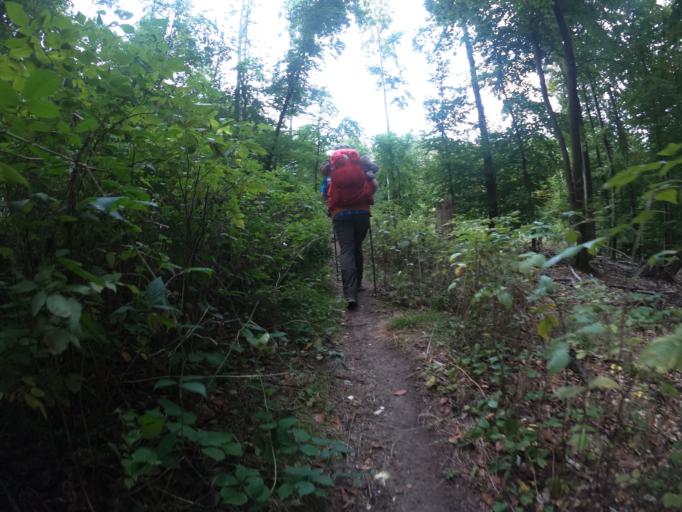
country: DE
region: Hesse
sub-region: Regierungsbezirk Darmstadt
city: Niedernhausen
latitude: 50.1538
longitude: 8.2998
